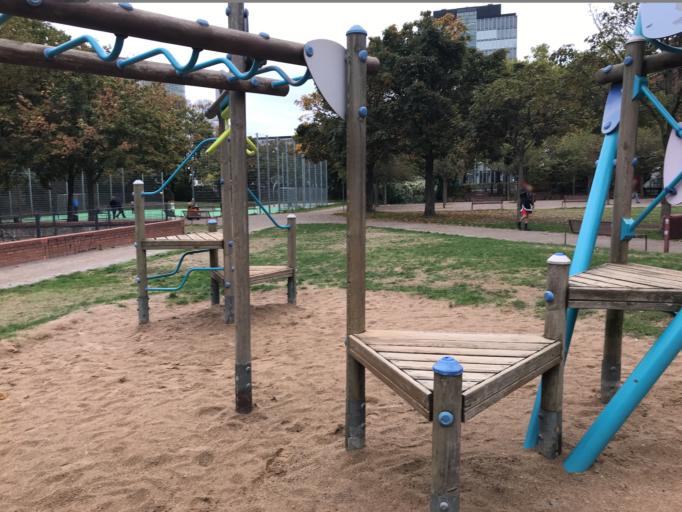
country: DE
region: North Rhine-Westphalia
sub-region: Regierungsbezirk Koln
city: Altstadt Sud
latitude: 50.9254
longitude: 6.9632
